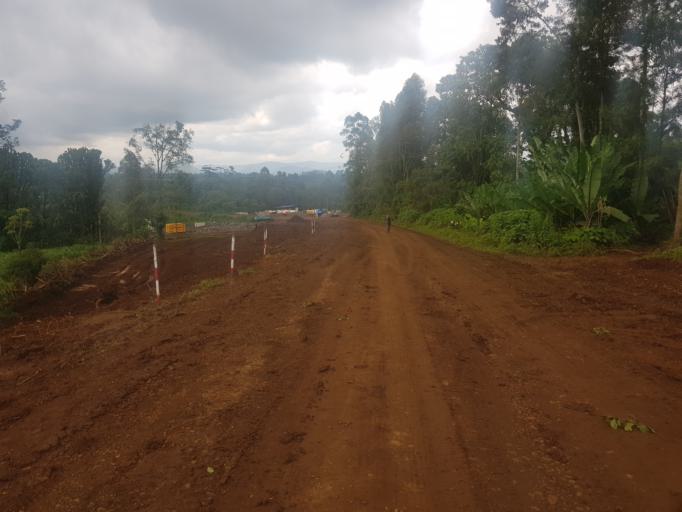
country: ET
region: Oromiya
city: Gore
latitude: 7.9211
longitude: 35.5167
